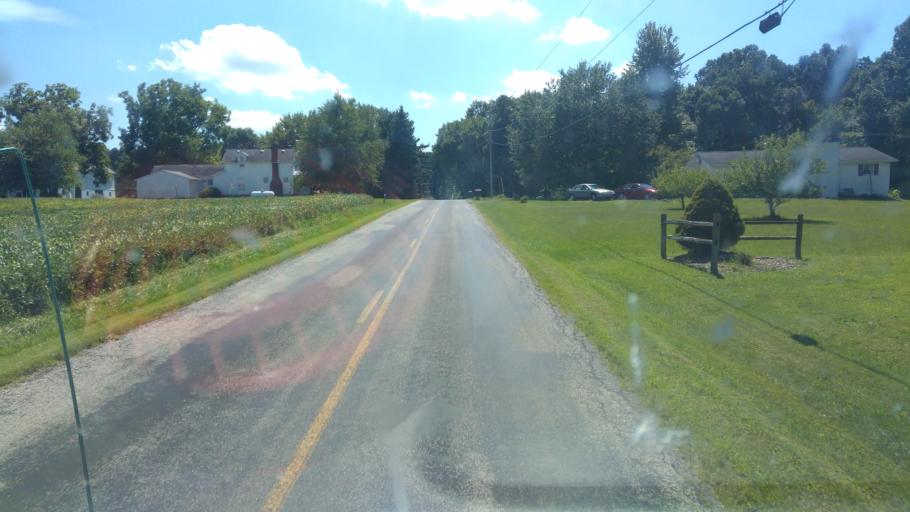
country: US
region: Ohio
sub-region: Marion County
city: Marion
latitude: 40.6691
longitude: -83.1733
